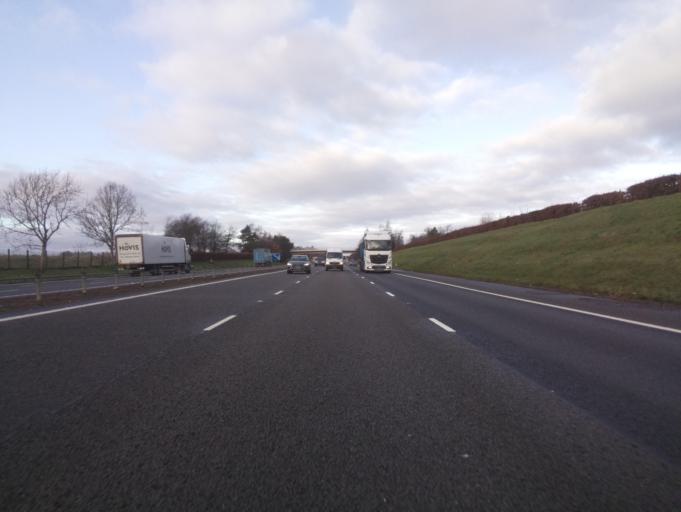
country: GB
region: Scotland
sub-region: Dumfries and Galloway
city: Lockerbie
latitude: 55.1126
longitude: -3.3563
